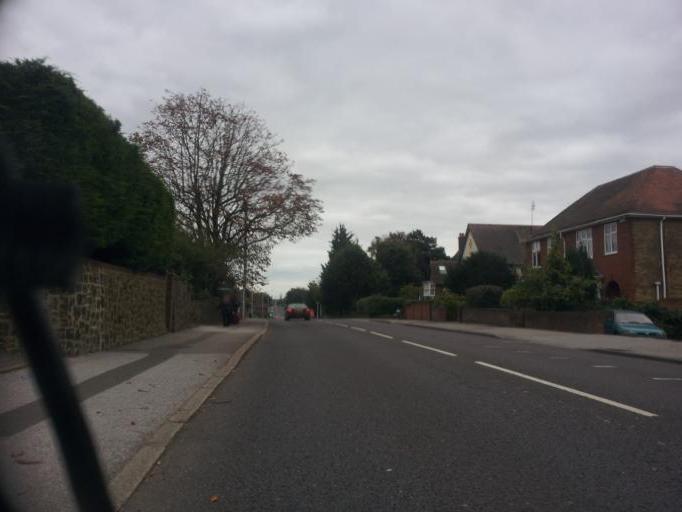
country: GB
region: England
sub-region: Kent
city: Sittingbourne
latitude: 51.3427
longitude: 0.7200
